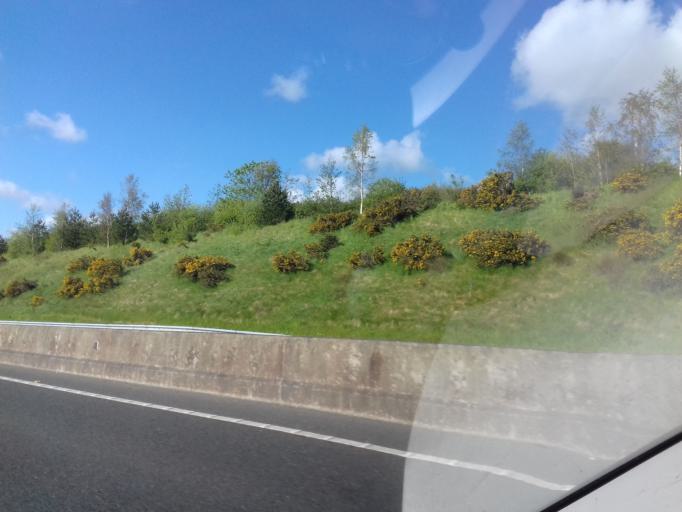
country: IE
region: Munster
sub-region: Waterford
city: Waterford
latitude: 52.3216
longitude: -7.1456
